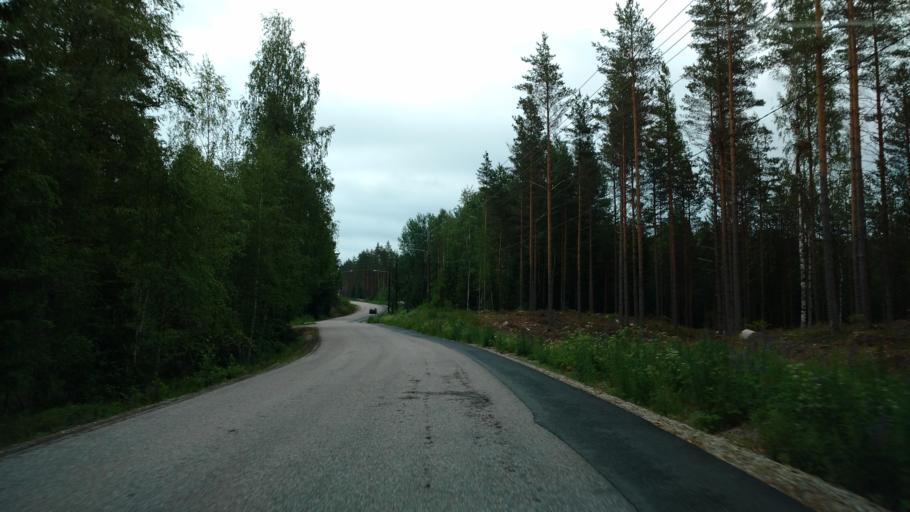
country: FI
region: Varsinais-Suomi
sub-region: Salo
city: Kiikala
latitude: 60.4304
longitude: 23.5956
